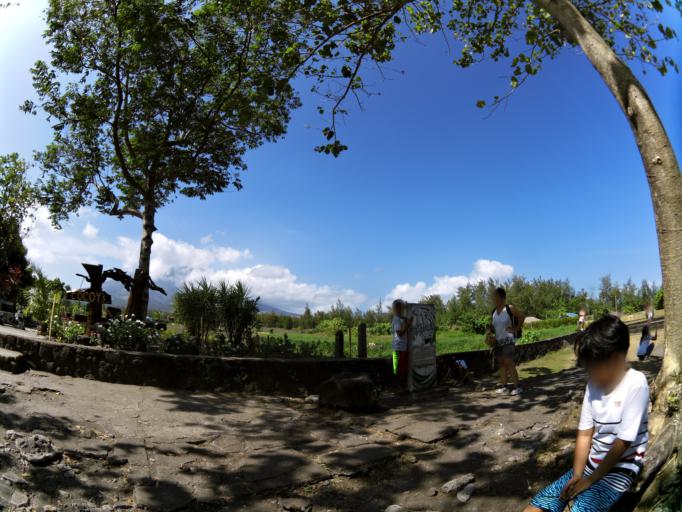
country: PH
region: Bicol
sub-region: Province of Albay
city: Malabog
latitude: 13.1665
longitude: 123.7007
